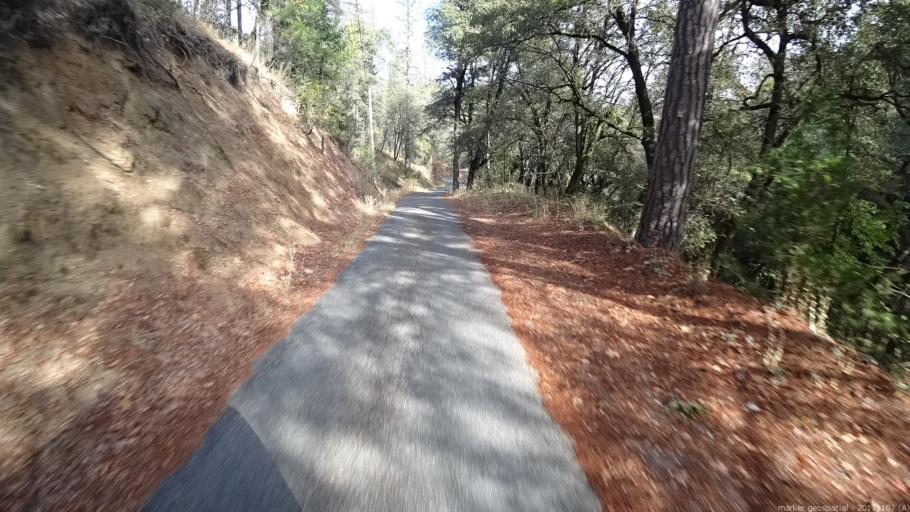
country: US
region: California
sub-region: Shasta County
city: Shasta
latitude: 40.5438
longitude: -122.5802
